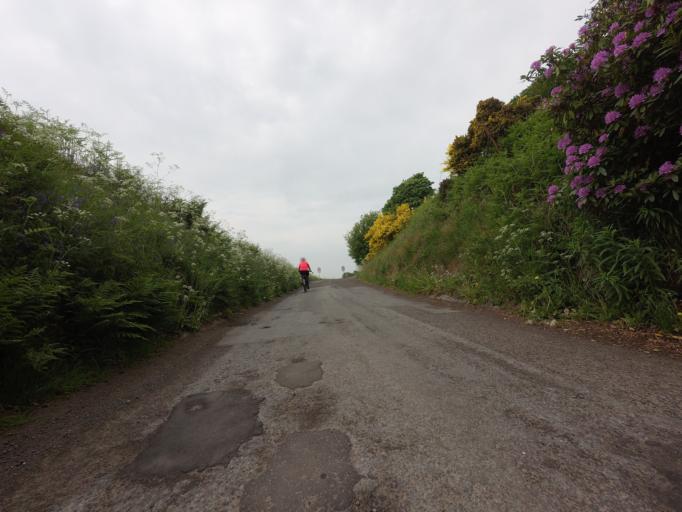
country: GB
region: Scotland
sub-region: Fife
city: Ballingry
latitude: 56.2287
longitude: -3.3418
